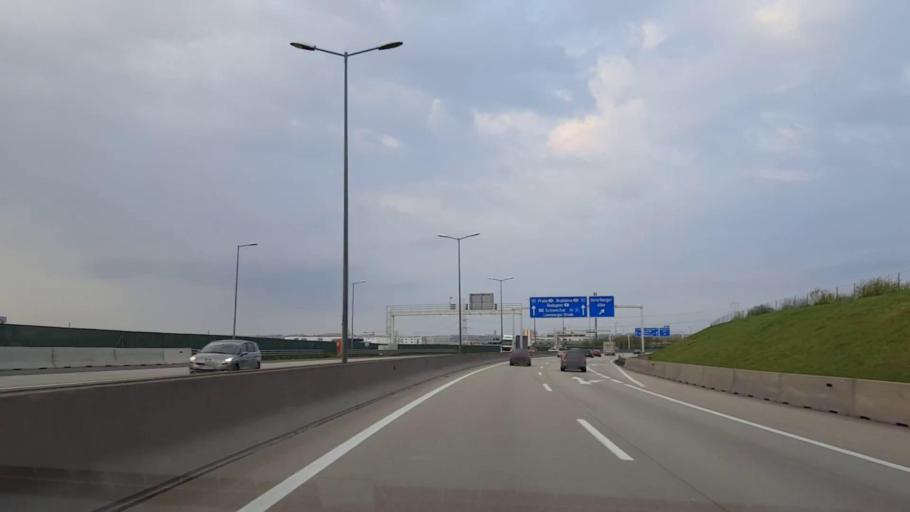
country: AT
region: Lower Austria
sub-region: Politischer Bezirk Modling
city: Vosendorf
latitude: 48.1304
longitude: 16.3342
